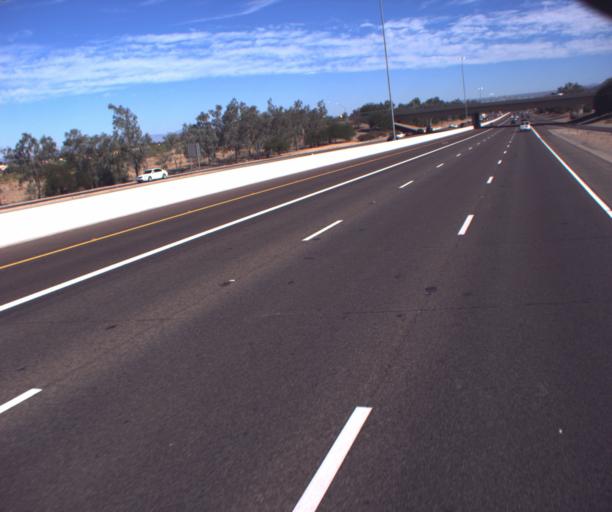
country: US
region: Arizona
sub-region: Maricopa County
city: Sun City
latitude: 33.6413
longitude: -112.2361
